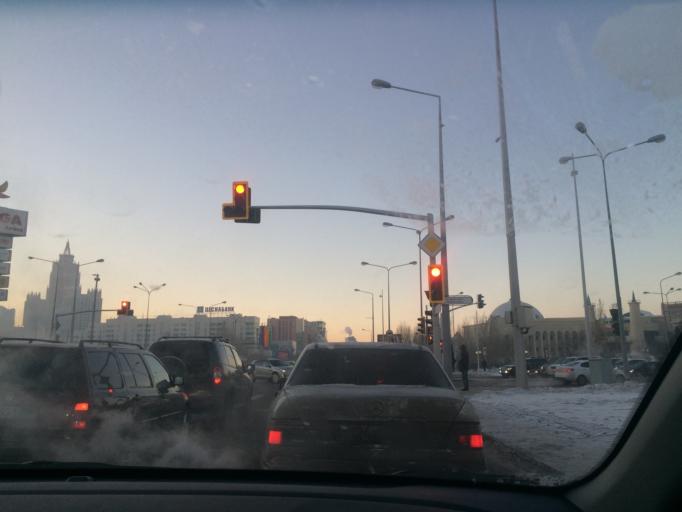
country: KZ
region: Astana Qalasy
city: Astana
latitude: 51.1464
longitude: 71.4119
